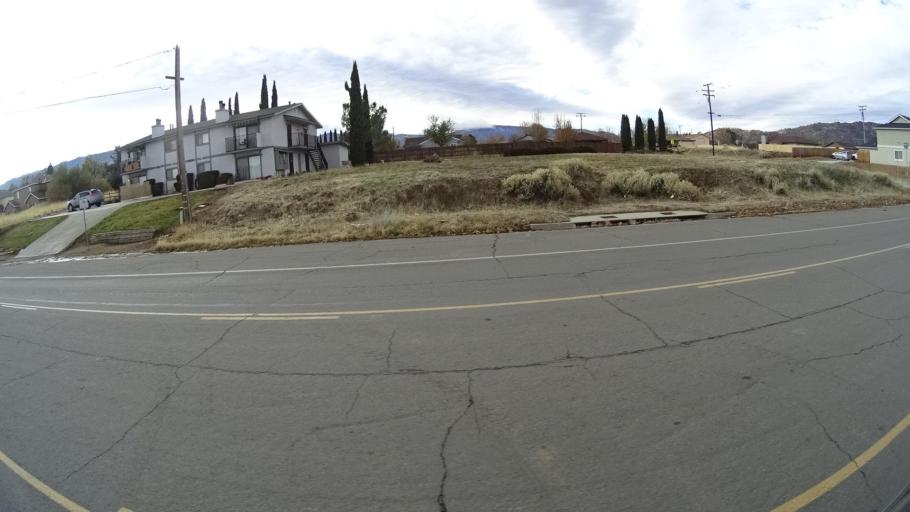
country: US
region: California
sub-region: Kern County
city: Golden Hills
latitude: 35.1315
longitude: -118.4883
